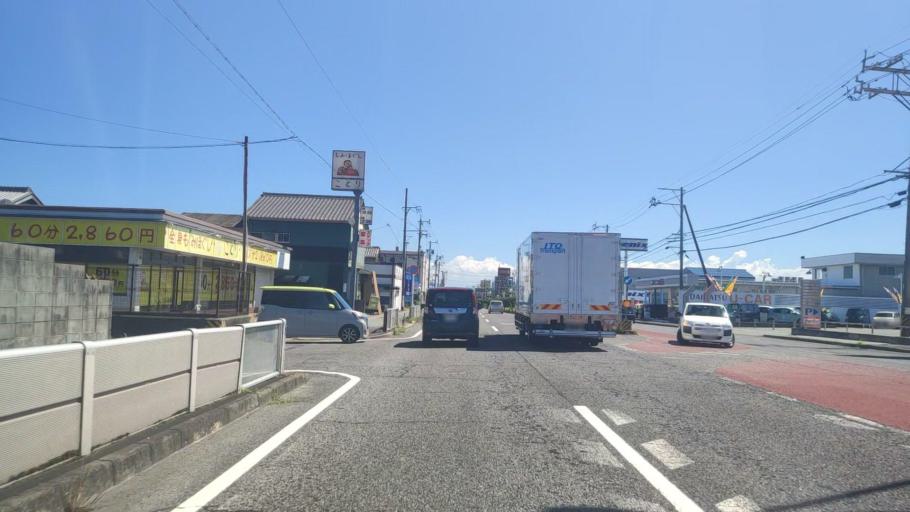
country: JP
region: Mie
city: Tsu-shi
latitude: 34.7534
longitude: 136.5223
